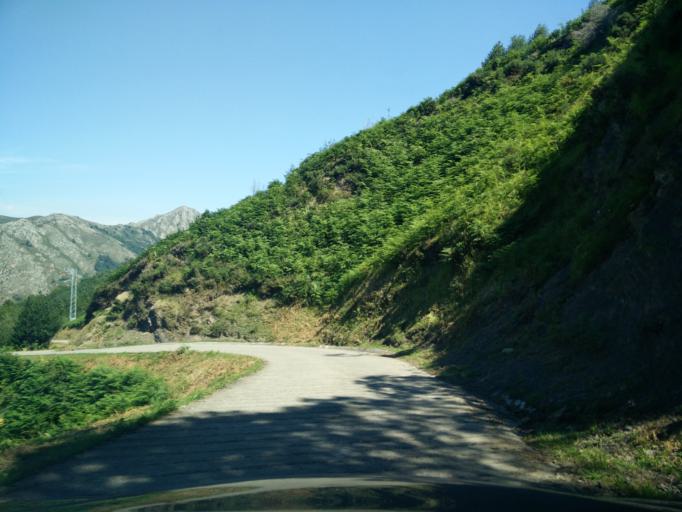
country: ES
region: Asturias
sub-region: Province of Asturias
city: Amieva
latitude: 43.1892
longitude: -5.1431
